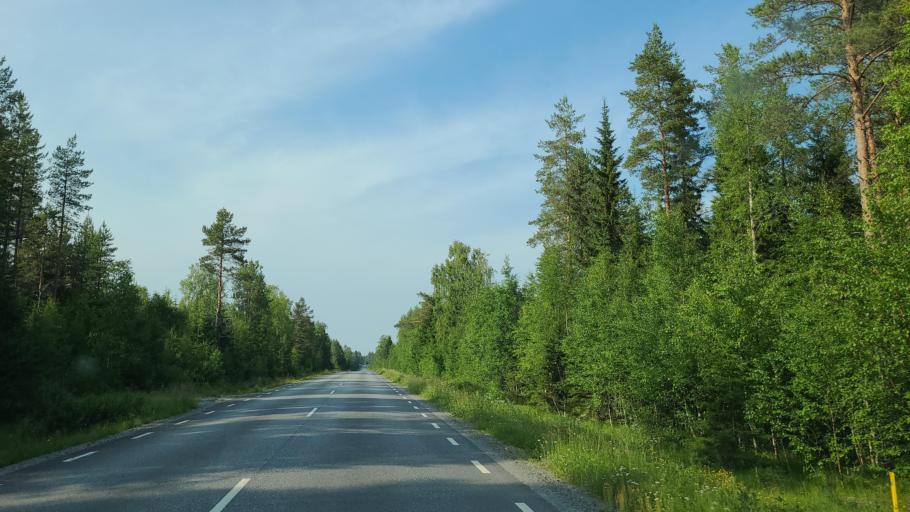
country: SE
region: Vaesterbotten
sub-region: Skelleftea Kommun
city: Burea
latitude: 64.4334
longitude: 21.3539
